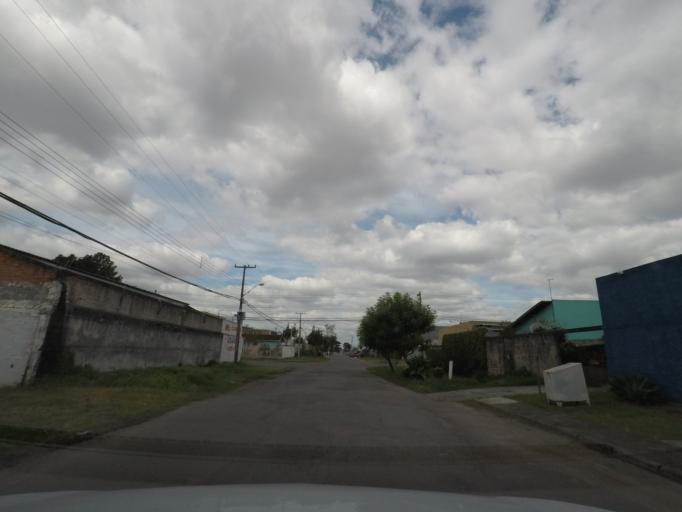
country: BR
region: Parana
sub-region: Sao Jose Dos Pinhais
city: Sao Jose dos Pinhais
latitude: -25.4862
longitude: -49.2396
